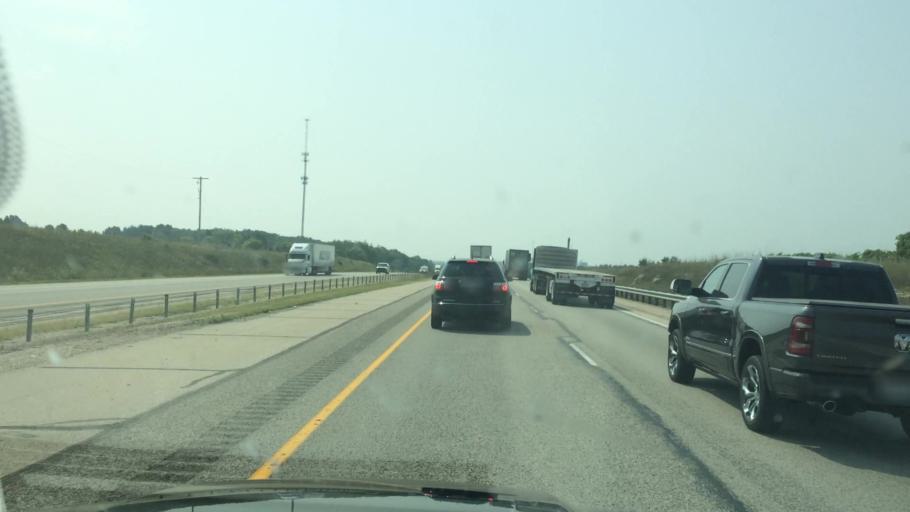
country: US
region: Wisconsin
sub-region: Dodge County
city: Lomira
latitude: 43.6590
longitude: -88.4416
